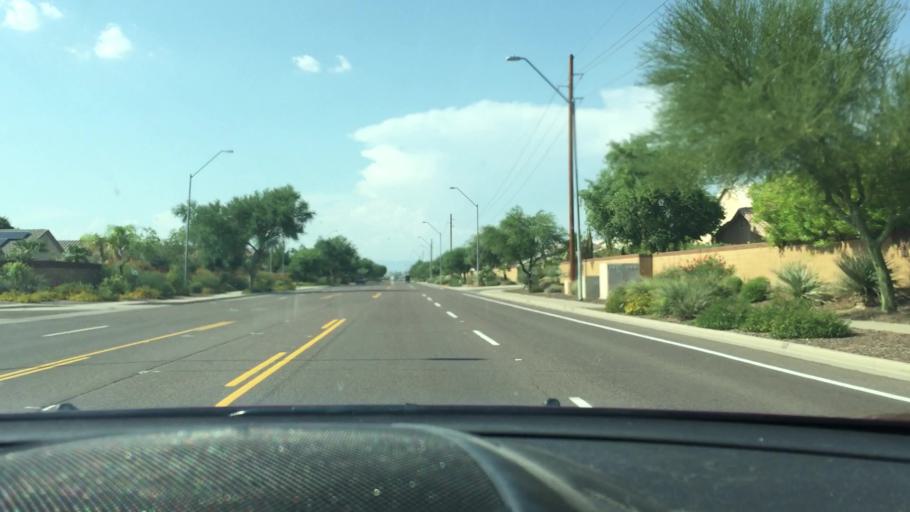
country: US
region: Arizona
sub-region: Maricopa County
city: Sun City
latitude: 33.6756
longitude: -112.2551
